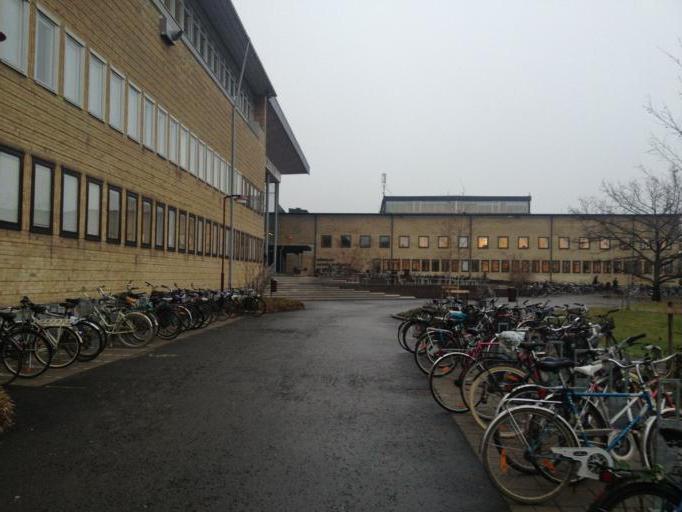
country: SE
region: Vaesterbotten
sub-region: Umea Kommun
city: Umea
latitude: 63.8215
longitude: 20.3044
